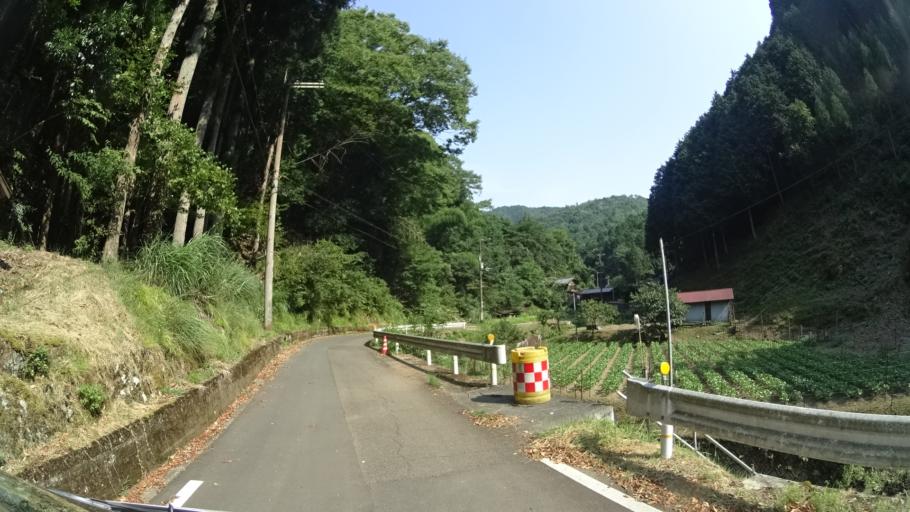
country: JP
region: Kyoto
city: Maizuru
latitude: 35.4027
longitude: 135.2418
